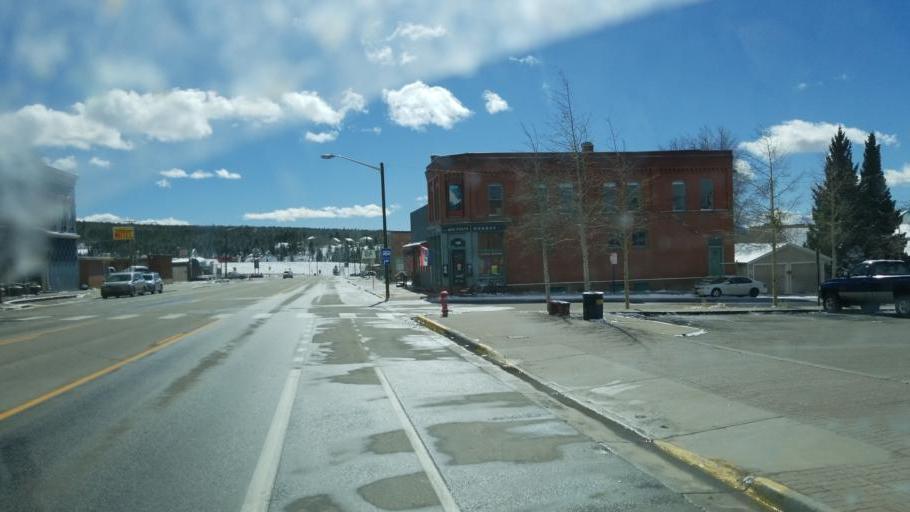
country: US
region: Colorado
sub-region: Lake County
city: Leadville
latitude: 39.2465
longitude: -106.2911
